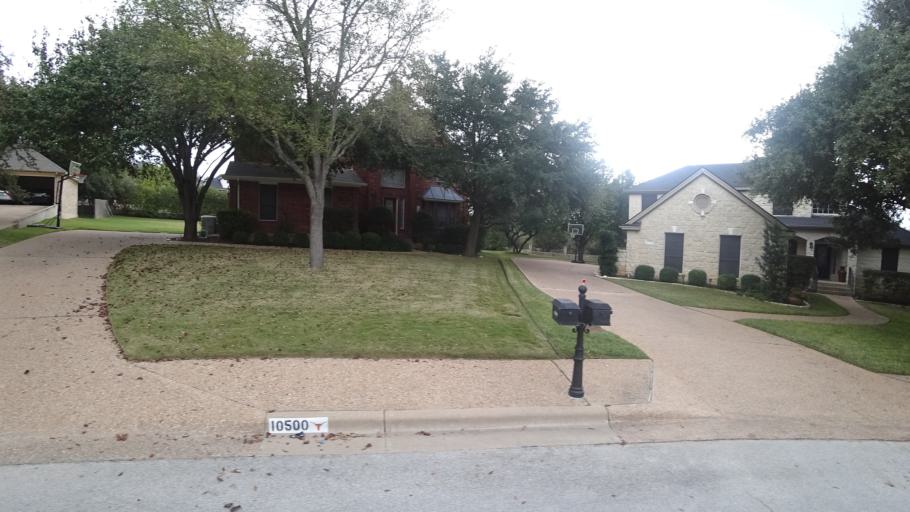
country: US
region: Texas
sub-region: Travis County
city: Barton Creek
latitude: 30.3098
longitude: -97.8979
